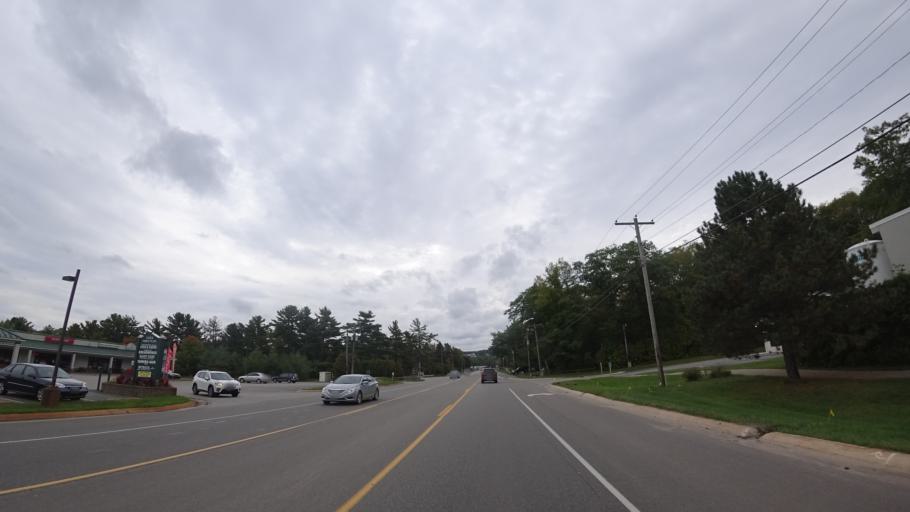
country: US
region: Michigan
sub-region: Emmet County
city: Petoskey
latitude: 45.4033
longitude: -84.9021
